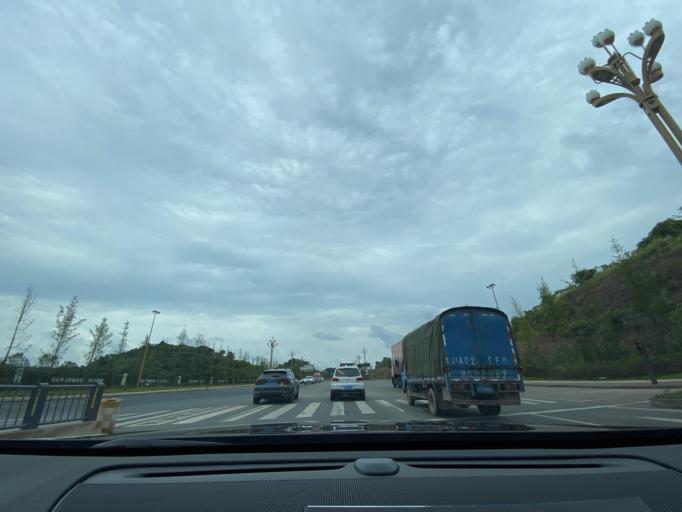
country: CN
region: Sichuan
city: Jiancheng
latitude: 30.4760
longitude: 104.4890
